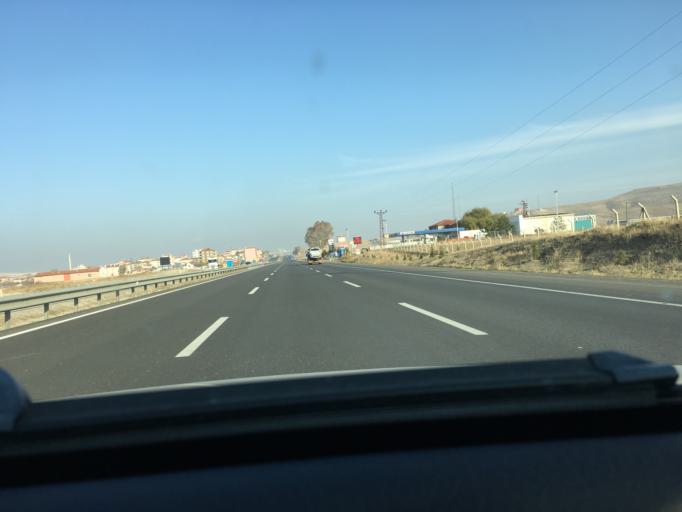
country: TR
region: Ankara
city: Temelli
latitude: 39.7217
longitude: 32.3391
